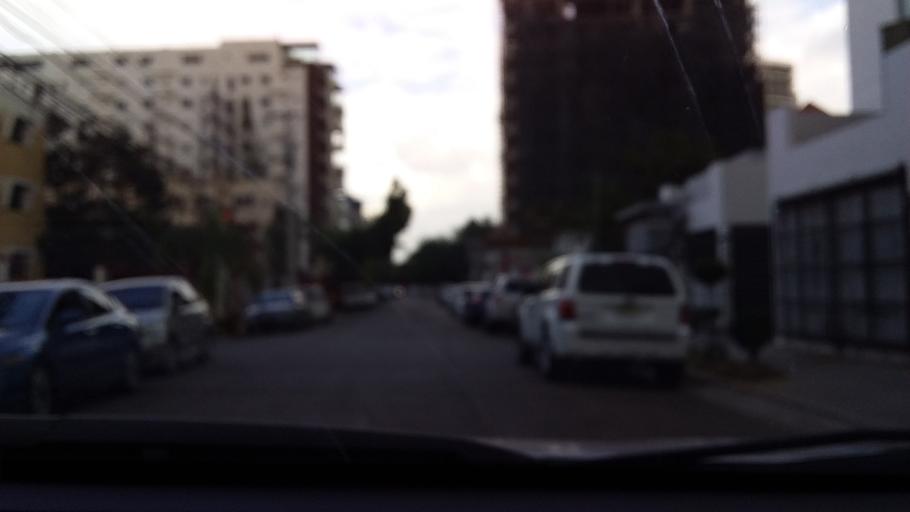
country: DO
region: Nacional
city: La Julia
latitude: 18.4583
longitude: -69.9353
